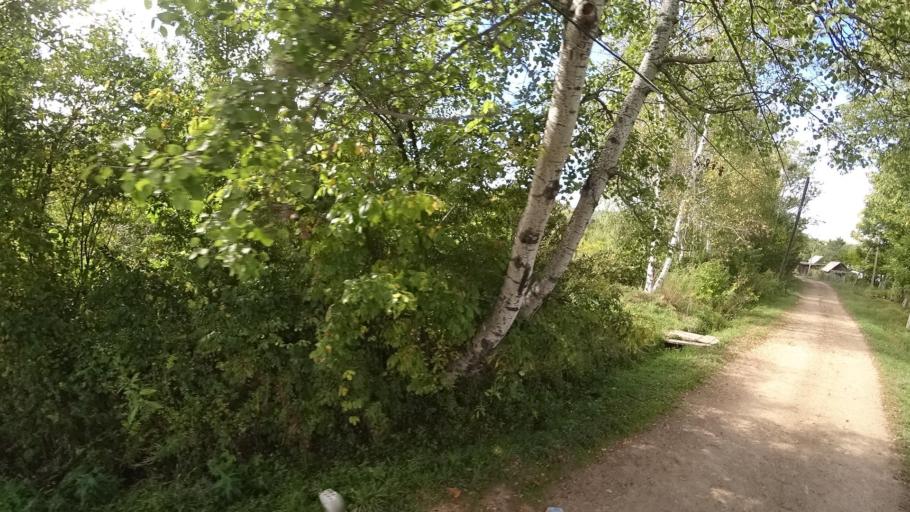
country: RU
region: Primorskiy
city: Yakovlevka
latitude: 44.3887
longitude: 133.6069
